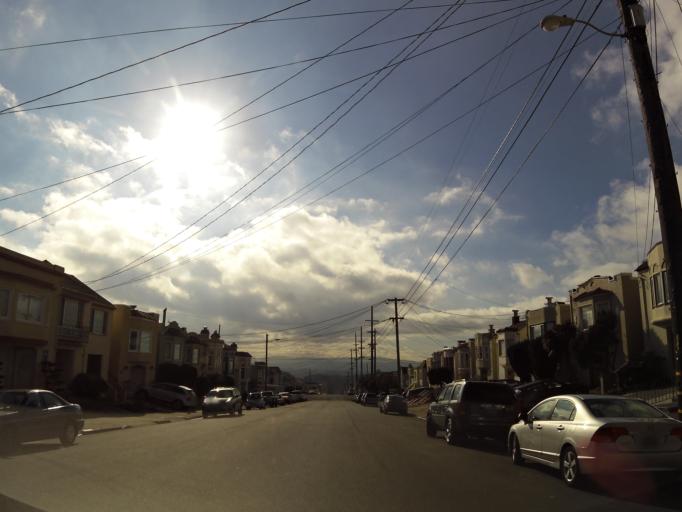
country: US
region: California
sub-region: San Mateo County
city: Daly City
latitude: 37.7481
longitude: -122.4772
